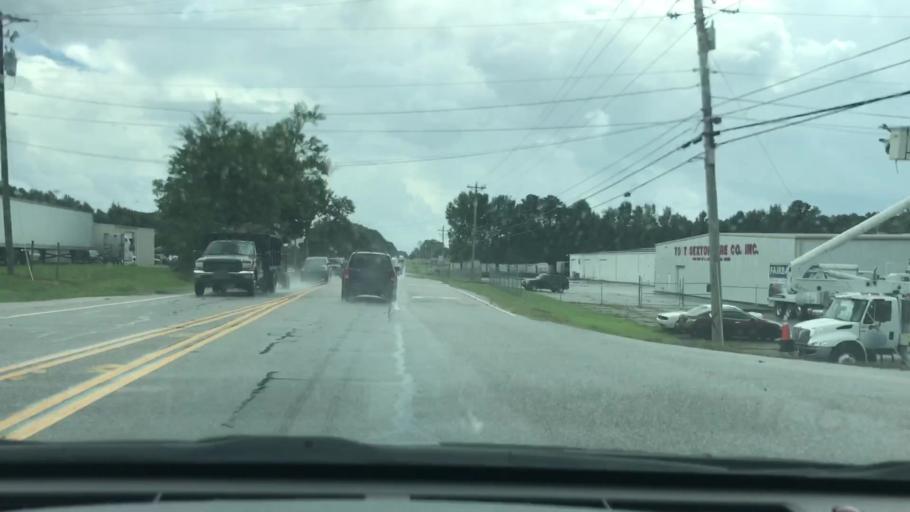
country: US
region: Georgia
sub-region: Walton County
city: Walnut Grove
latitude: 33.7779
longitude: -83.8525
